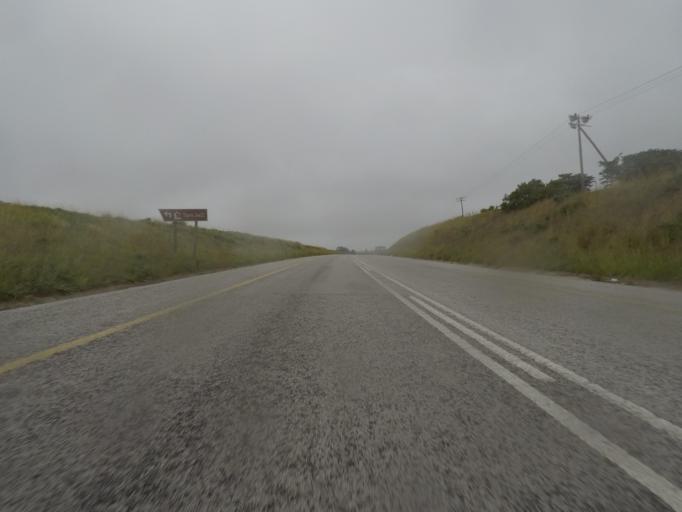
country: ZA
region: Eastern Cape
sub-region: Cacadu District Municipality
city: Grahamstown
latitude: -33.6436
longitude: 26.3492
